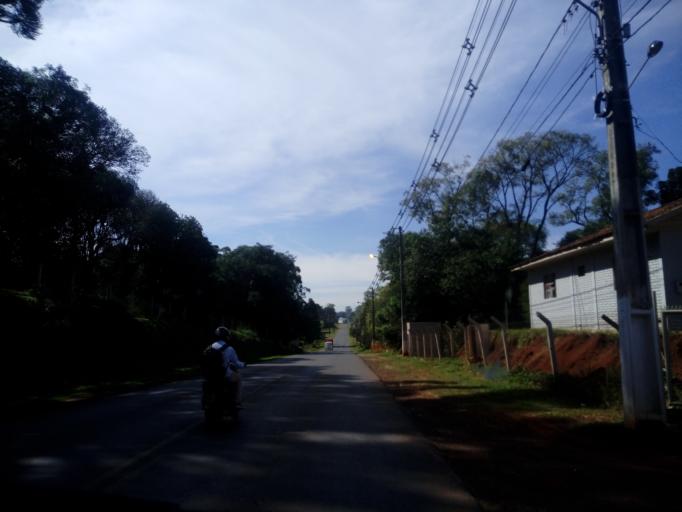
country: BR
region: Santa Catarina
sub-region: Chapeco
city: Chapeco
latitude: -27.0890
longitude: -52.6621
